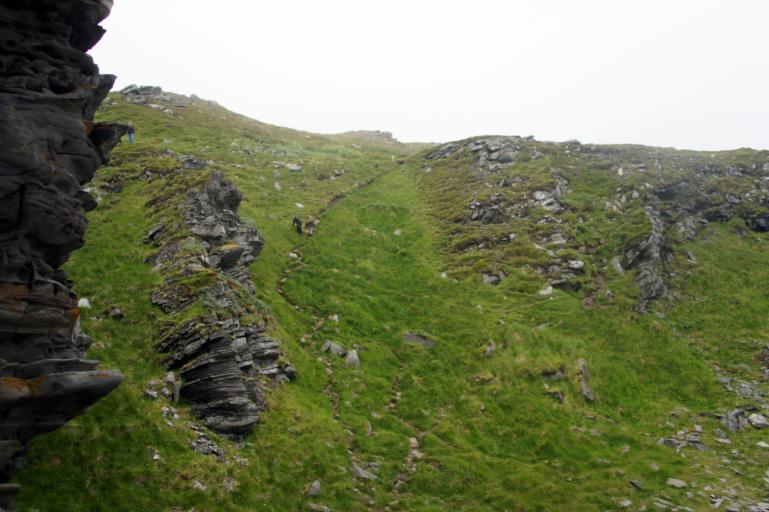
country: NO
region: Finnmark Fylke
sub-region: Nordkapp
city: Honningsvag
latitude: 71.1134
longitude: 25.8026
